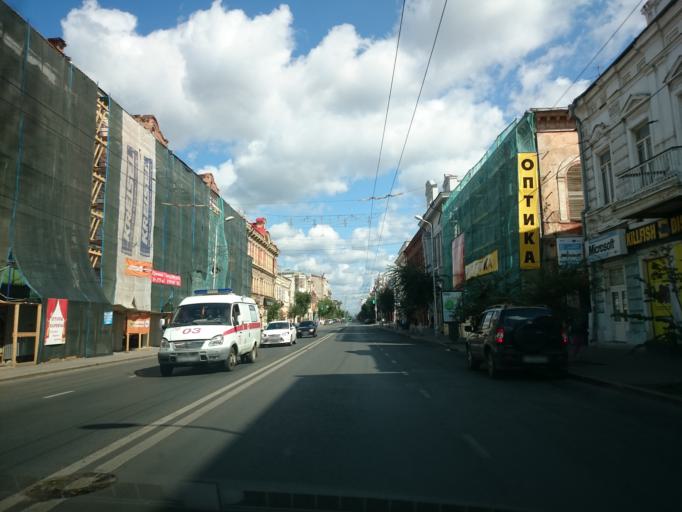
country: RU
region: Samara
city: Rozhdestveno
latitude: 53.1869
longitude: 50.0885
